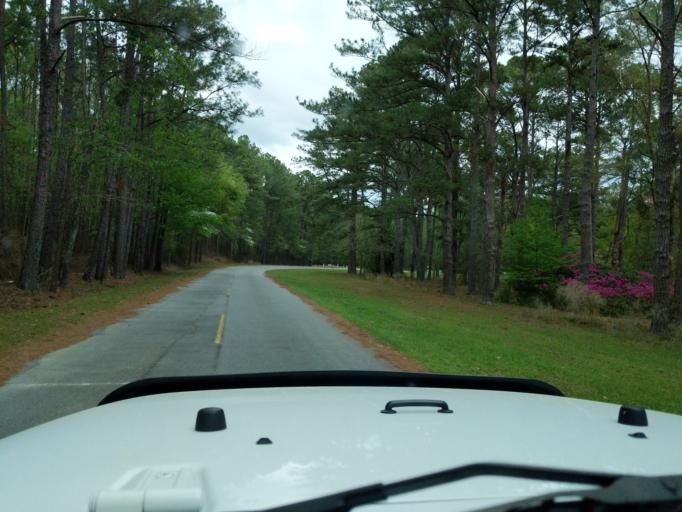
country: US
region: Georgia
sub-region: Clay County
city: Fort Gaines
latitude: 31.6736
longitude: -85.0634
